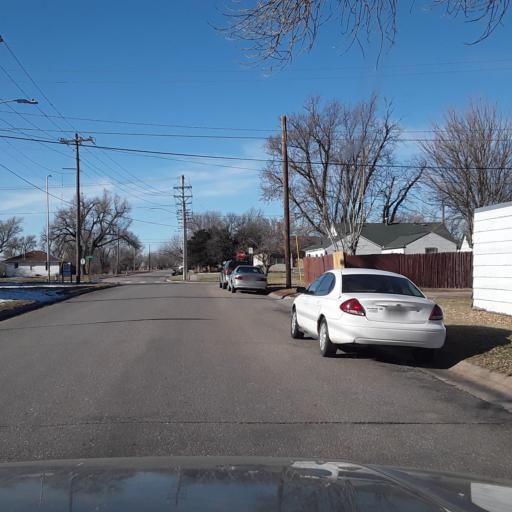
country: US
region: Nebraska
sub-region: Adams County
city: Hastings
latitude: 40.5771
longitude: -98.4010
